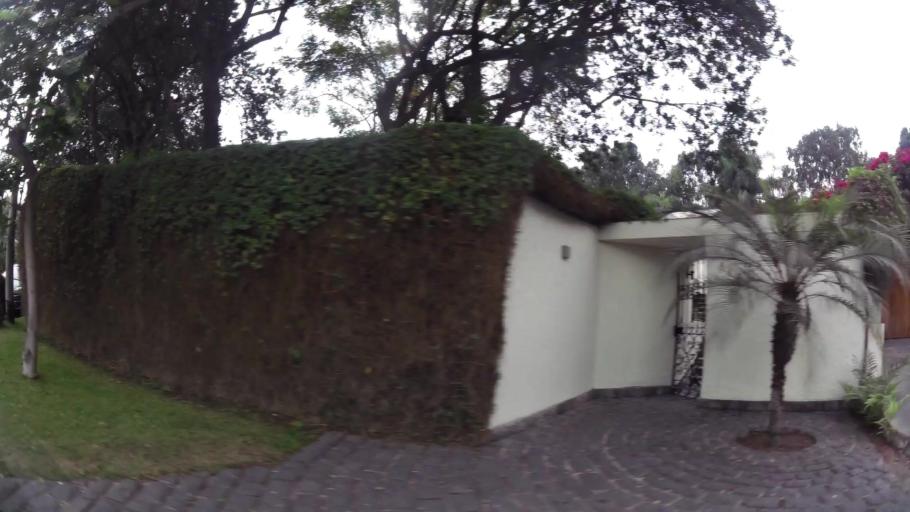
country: PE
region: Lima
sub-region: Lima
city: La Molina
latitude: -12.0783
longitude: -76.9281
